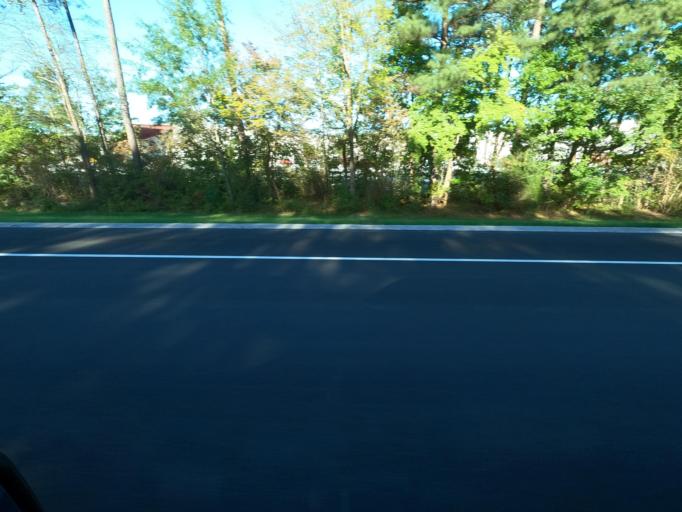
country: US
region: Tennessee
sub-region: Coffee County
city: Manchester
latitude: 35.4207
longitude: -86.0194
